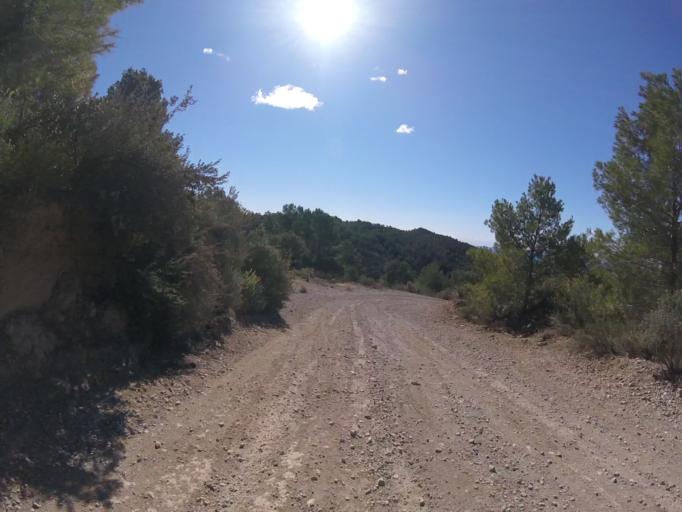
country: ES
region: Valencia
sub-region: Provincia de Castello
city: Benicassim
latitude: 40.0743
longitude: 0.0769
